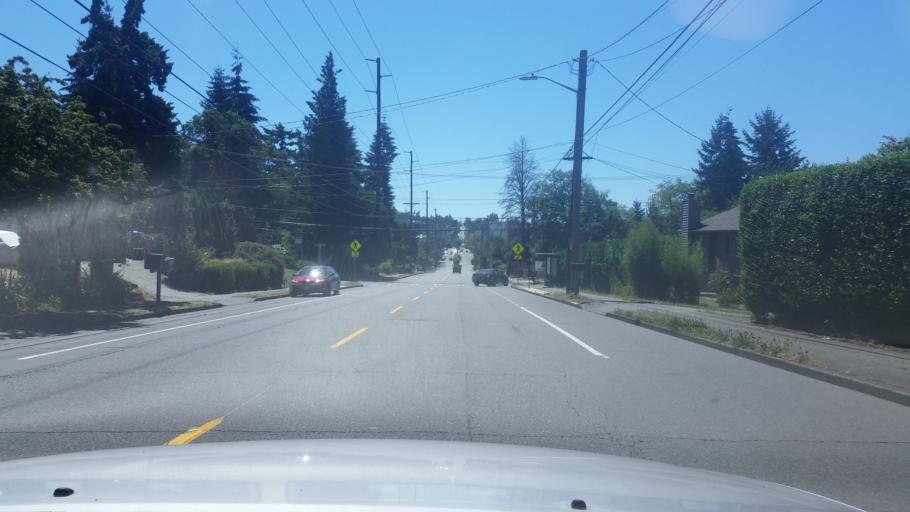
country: US
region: Washington
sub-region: King County
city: Shoreline
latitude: 47.7130
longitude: -122.3234
